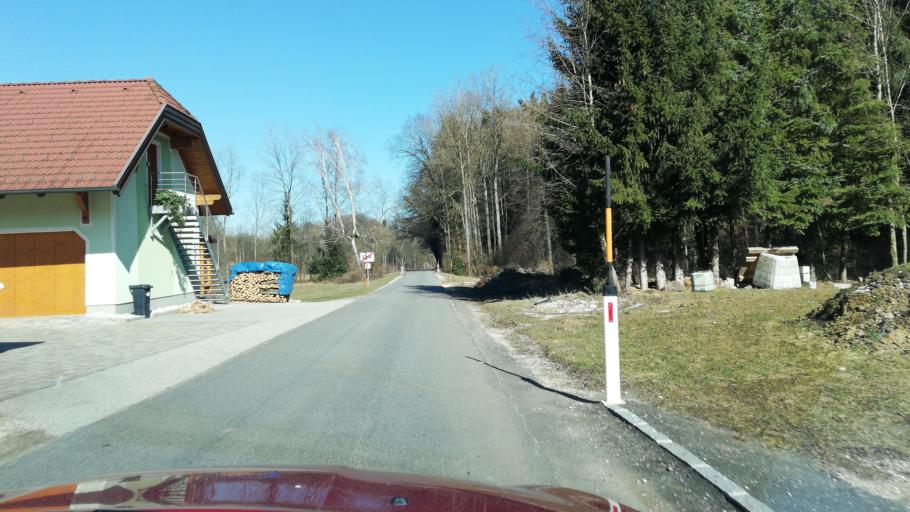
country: AT
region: Upper Austria
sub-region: Politischer Bezirk Vocklabruck
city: Aurach am Hongar
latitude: 47.9618
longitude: 13.6959
